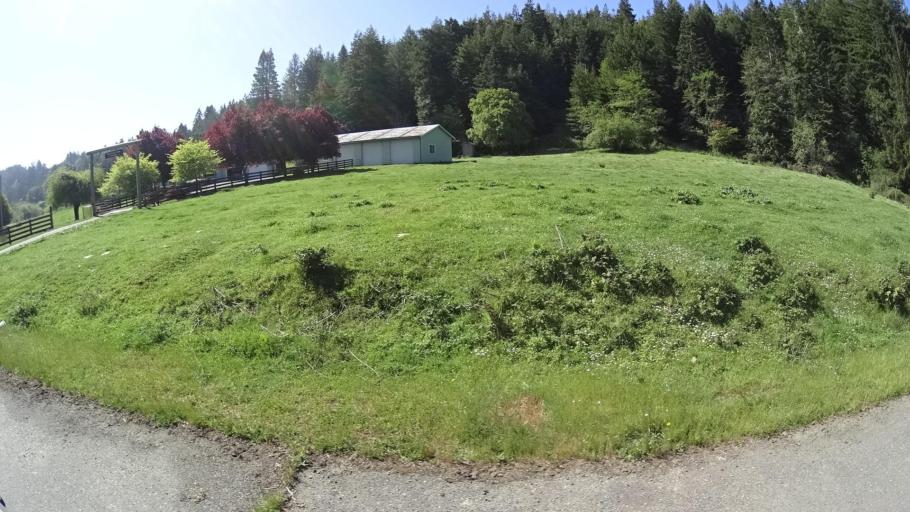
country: US
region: California
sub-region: Humboldt County
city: Fortuna
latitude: 40.5285
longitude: -124.1795
